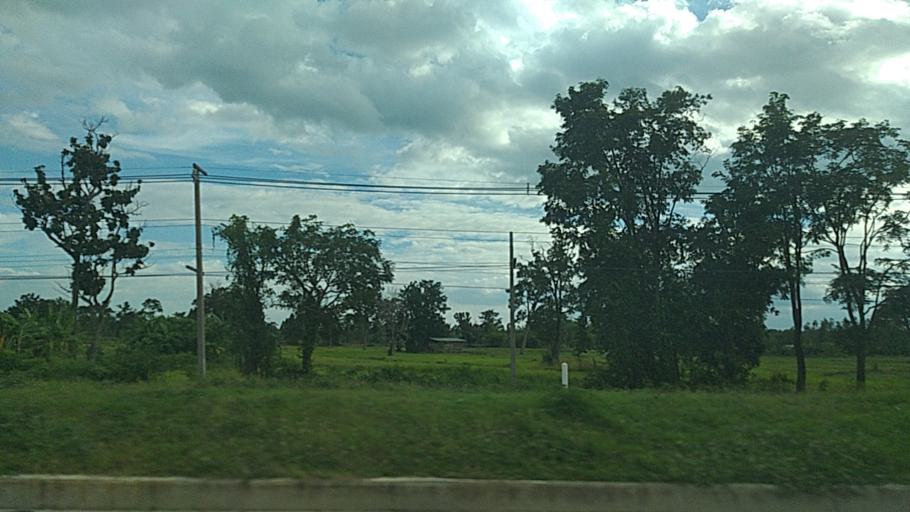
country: TH
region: Surin
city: Prasat
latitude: 14.5620
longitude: 103.4973
